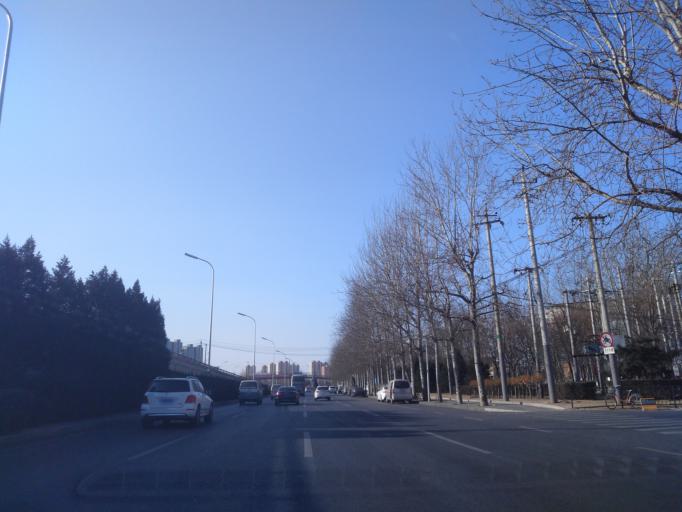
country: CN
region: Beijing
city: Jiugong
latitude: 39.8363
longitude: 116.4647
